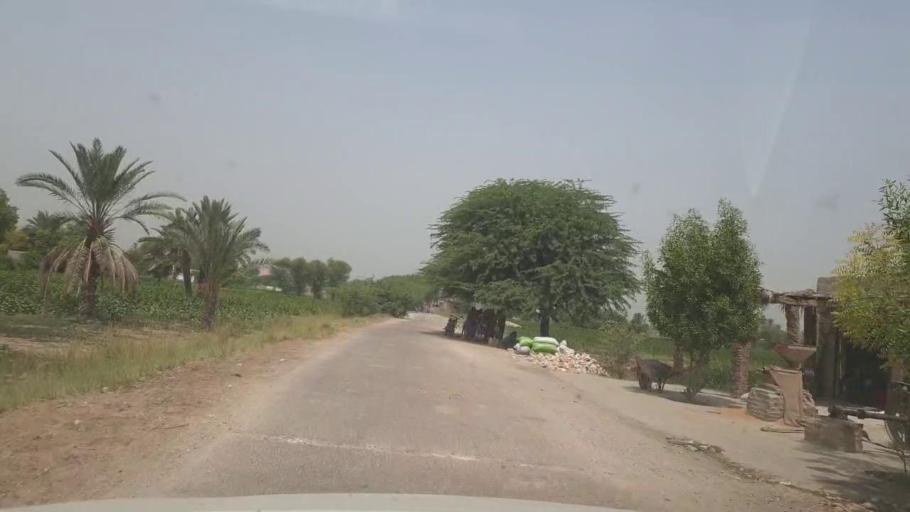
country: PK
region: Sindh
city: Kot Diji
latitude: 27.3628
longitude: 68.6704
